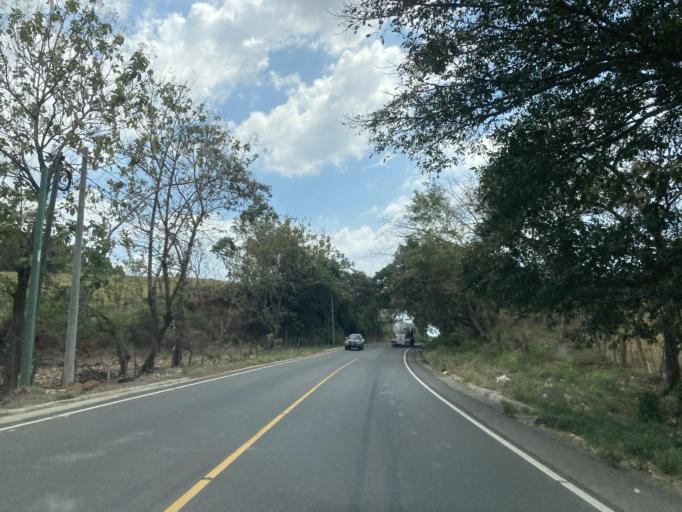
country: GT
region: Santa Rosa
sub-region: Municipio de Taxisco
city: Taxisco
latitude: 14.0833
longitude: -90.4910
